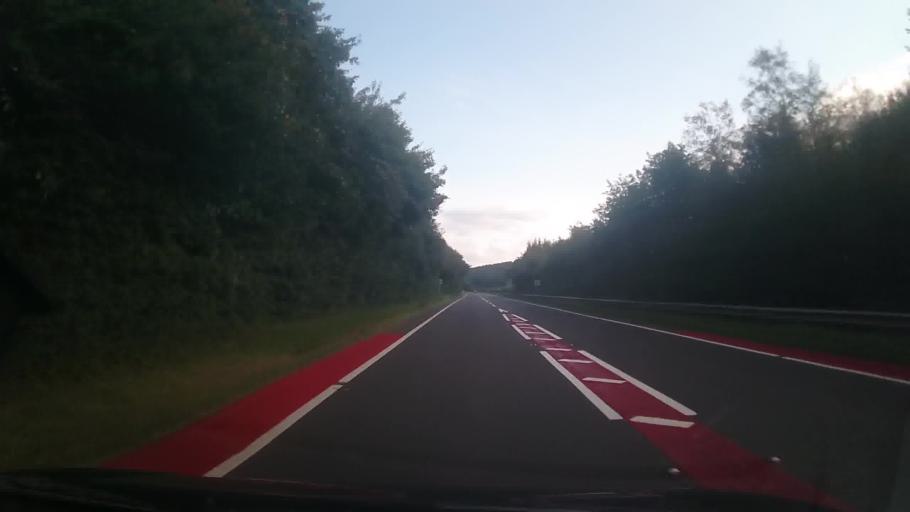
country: GB
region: England
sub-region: Shropshire
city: Craven Arms
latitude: 52.4237
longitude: -2.8240
